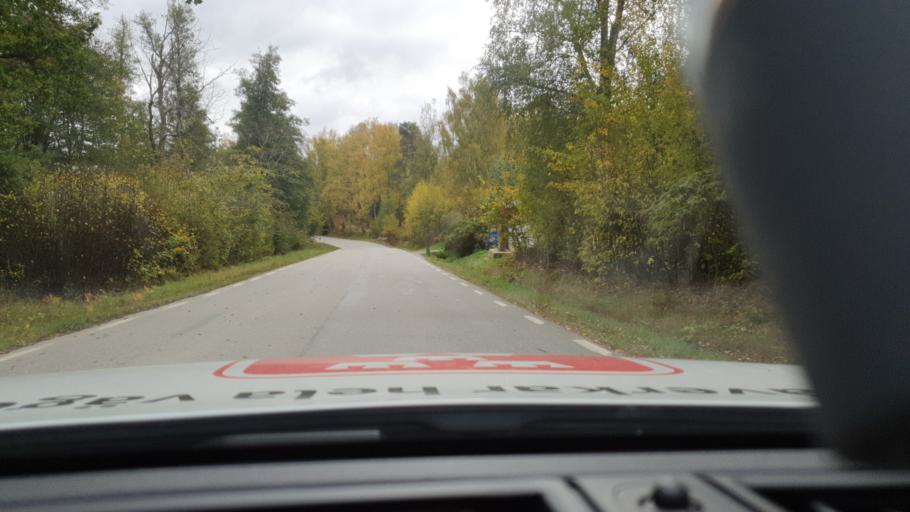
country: SE
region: Stockholm
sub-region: Upplands-Bro Kommun
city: Bro
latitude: 59.4977
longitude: 17.5684
